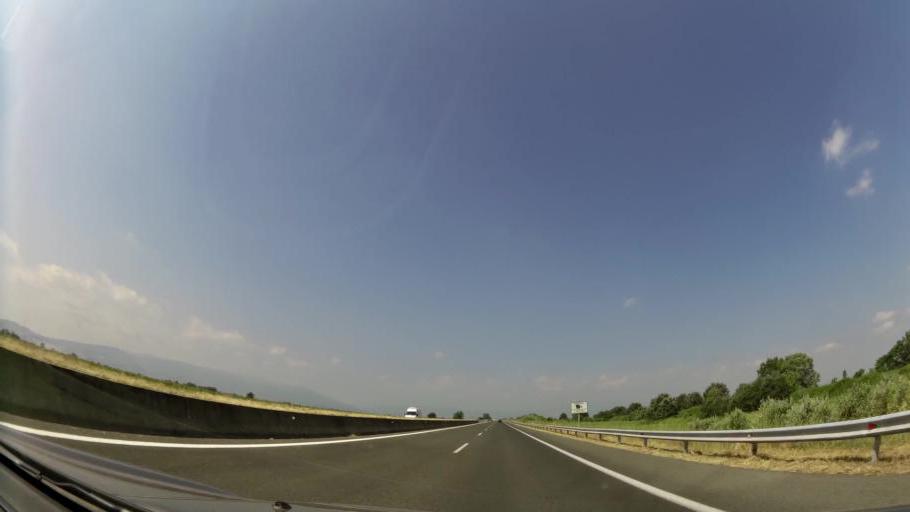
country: GR
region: Central Macedonia
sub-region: Nomos Imathias
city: Loutros
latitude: 40.5680
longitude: 22.3793
